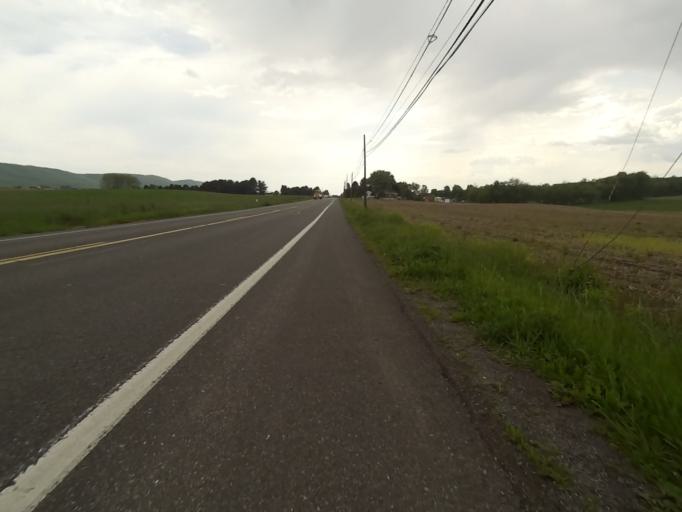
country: US
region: Pennsylvania
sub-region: Centre County
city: Zion
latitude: 40.9240
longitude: -77.6686
